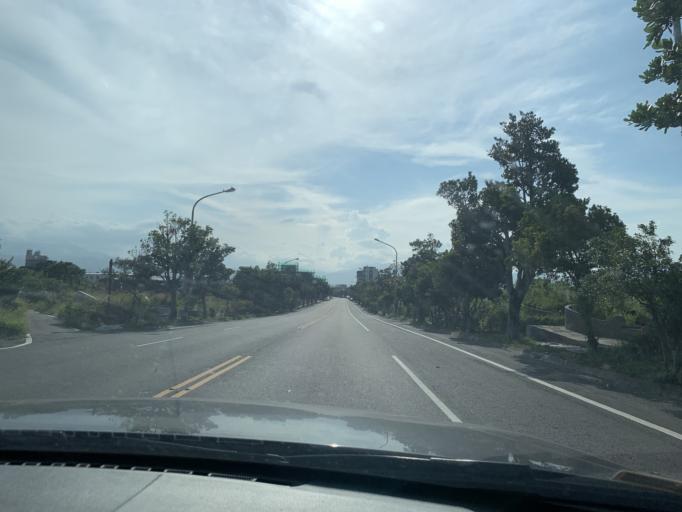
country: TW
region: Taiwan
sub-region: Yilan
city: Yilan
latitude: 24.6687
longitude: 121.8271
